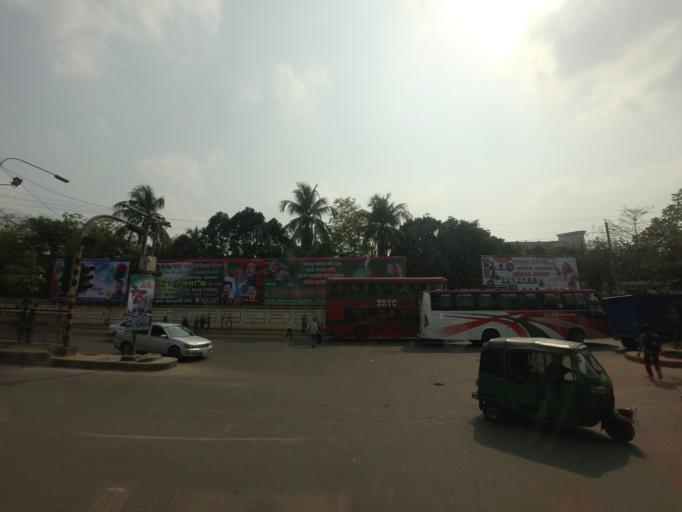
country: BD
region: Dhaka
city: Azimpur
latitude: 23.7816
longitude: 90.3519
